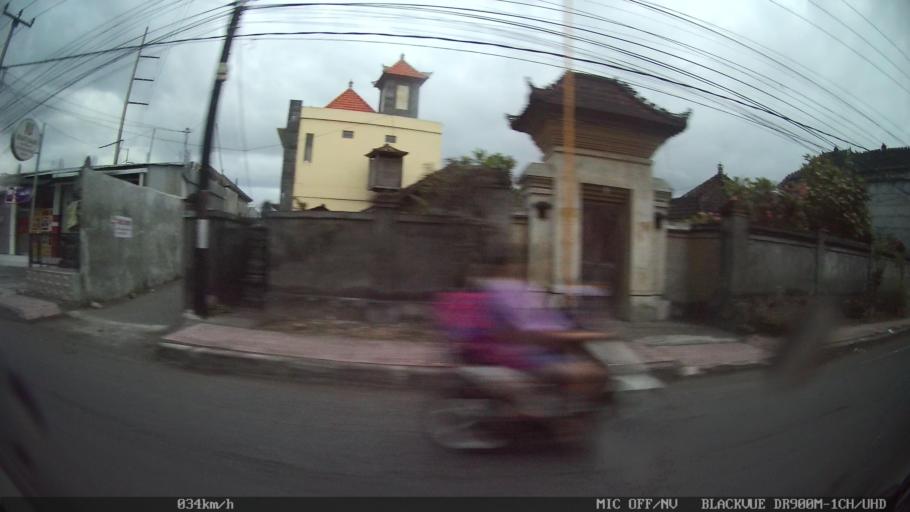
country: ID
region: Bali
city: Banjar Pasekan
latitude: -8.6354
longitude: 115.2830
